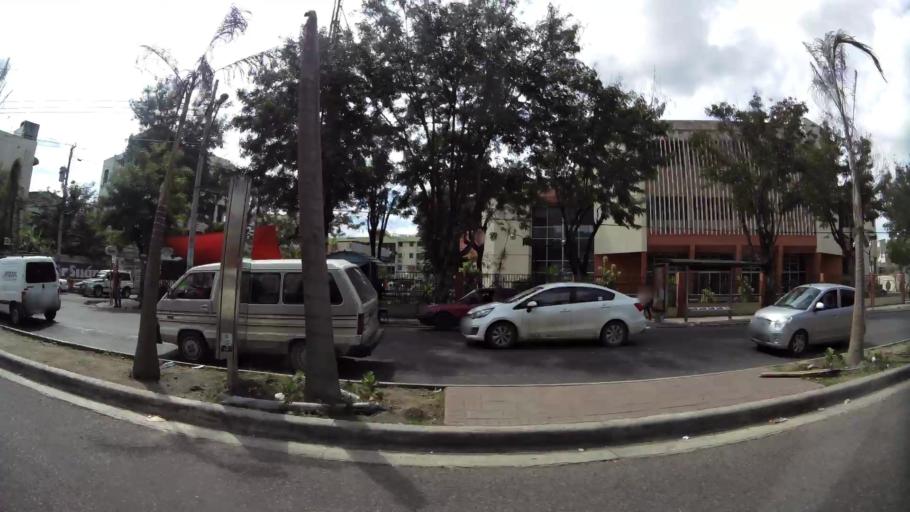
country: DO
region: Santiago
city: Santiago de los Caballeros
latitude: 19.4556
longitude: -70.7038
